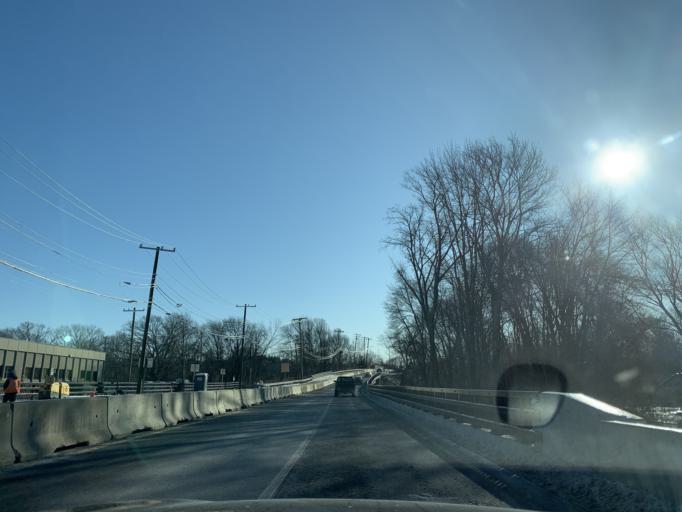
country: US
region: Massachusetts
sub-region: Norfolk County
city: Canton
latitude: 42.1978
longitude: -71.1562
